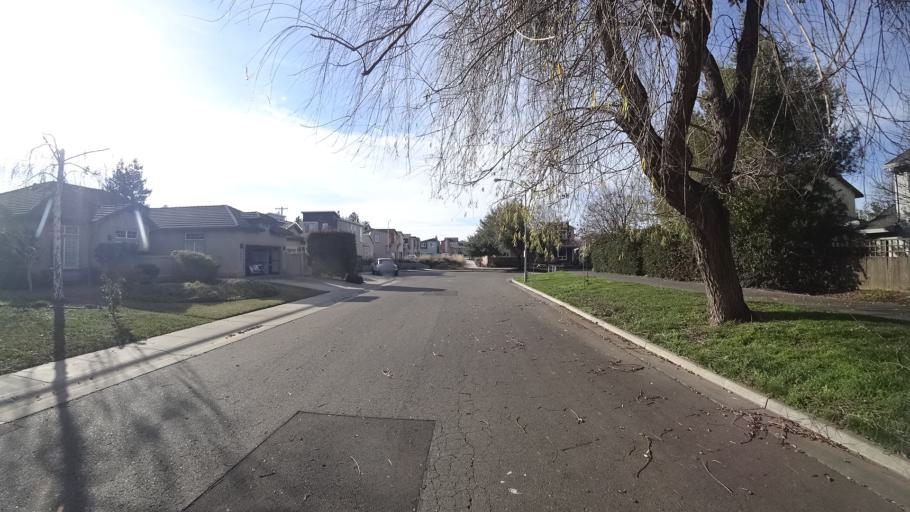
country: US
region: California
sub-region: Yolo County
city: Davis
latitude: 38.5465
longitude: -121.7111
